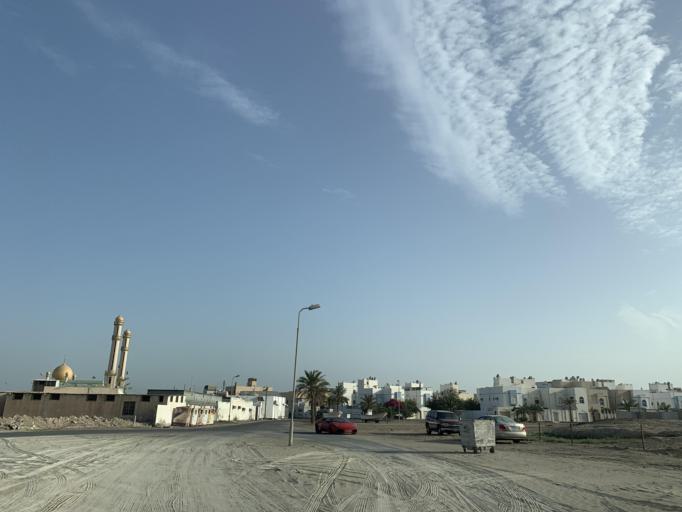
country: BH
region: Northern
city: Madinat `Isa
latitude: 26.1783
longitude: 50.5813
